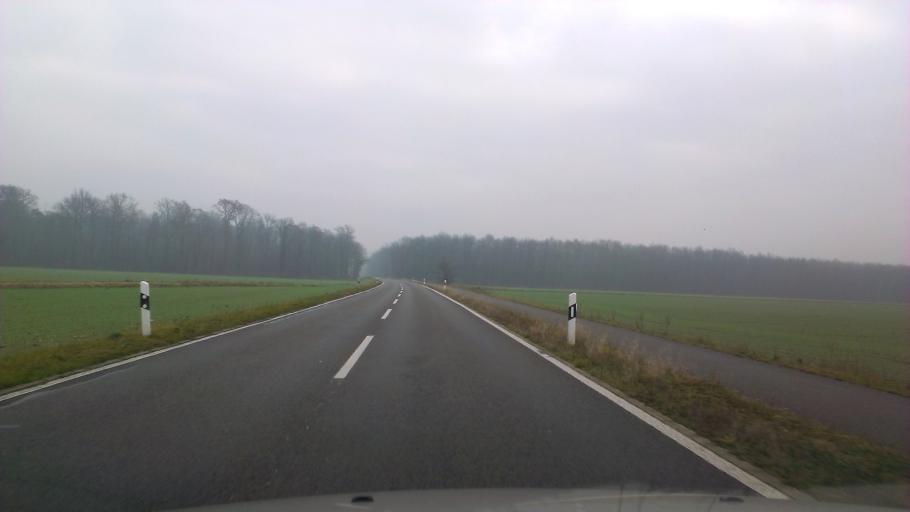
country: DE
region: Baden-Wuerttemberg
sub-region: Karlsruhe Region
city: Hambrucken
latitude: 49.1846
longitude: 8.5618
